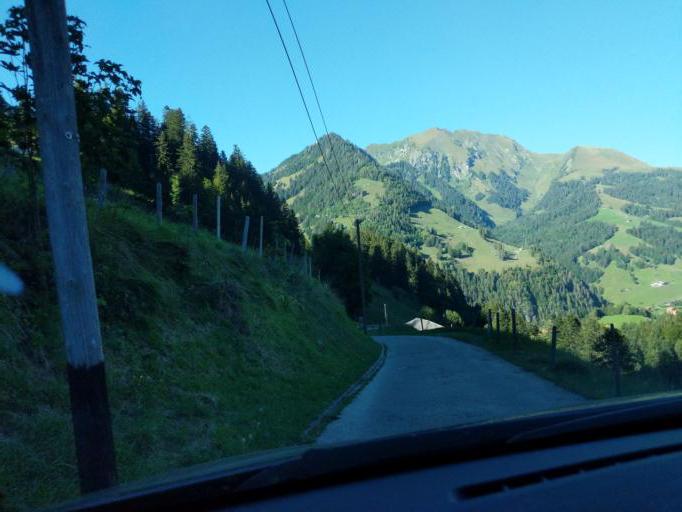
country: CH
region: Fribourg
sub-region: Gruyere District
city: Charmey
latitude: 46.6018
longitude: 7.2724
